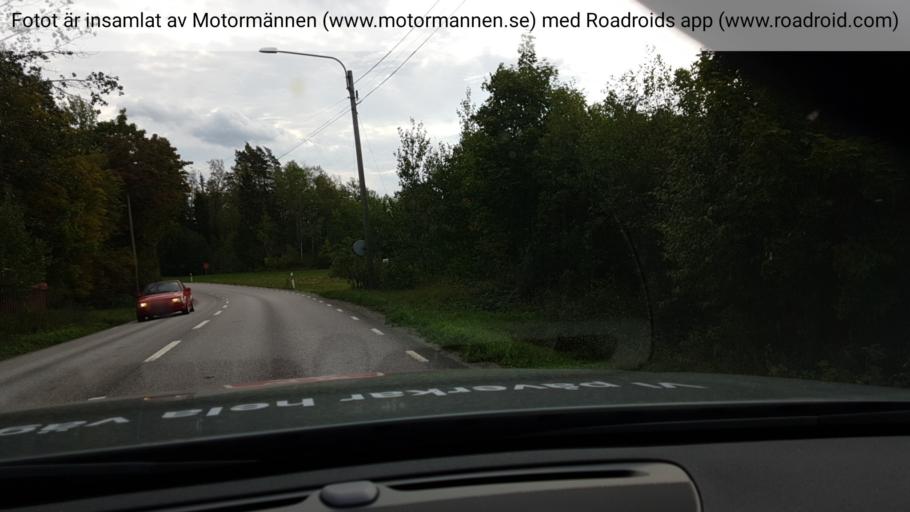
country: SE
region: Stockholm
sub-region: Norrtalje Kommun
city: Rimbo
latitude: 59.7335
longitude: 18.4159
